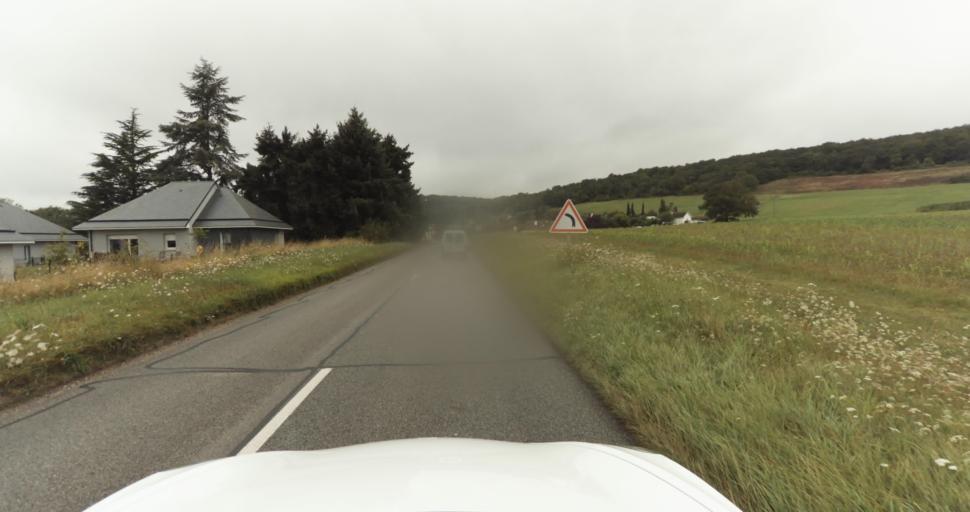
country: FR
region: Haute-Normandie
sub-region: Departement de l'Eure
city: Normanville
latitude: 49.0772
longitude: 1.1650
